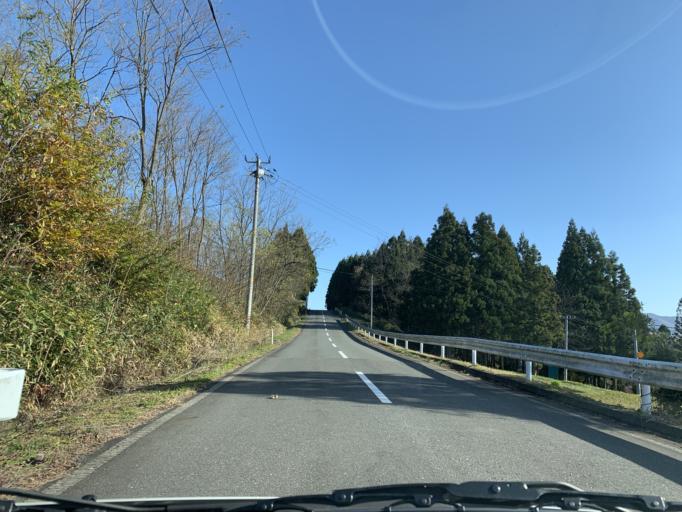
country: JP
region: Iwate
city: Mizusawa
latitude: 39.0729
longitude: 141.1133
